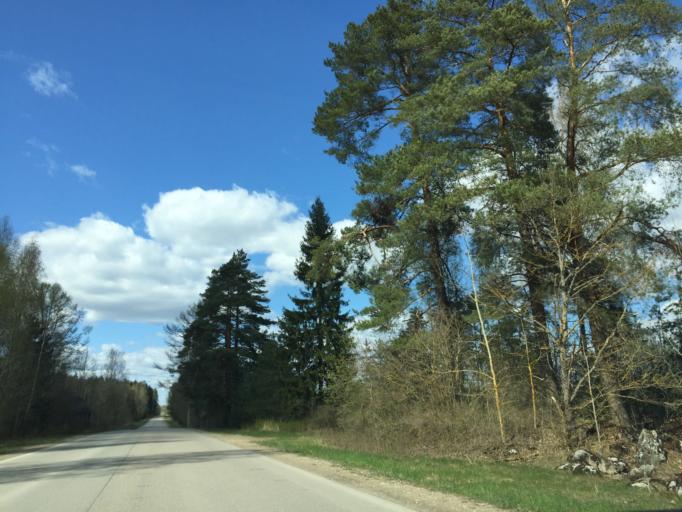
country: LV
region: Vilanu
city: Vilani
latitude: 56.5638
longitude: 27.0535
